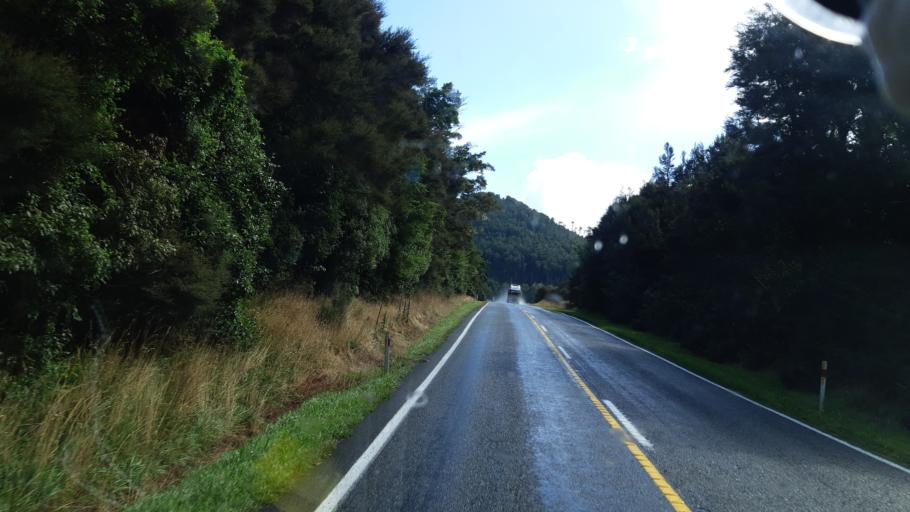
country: NZ
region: West Coast
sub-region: Buller District
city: Westport
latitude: -42.3530
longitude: 172.2311
